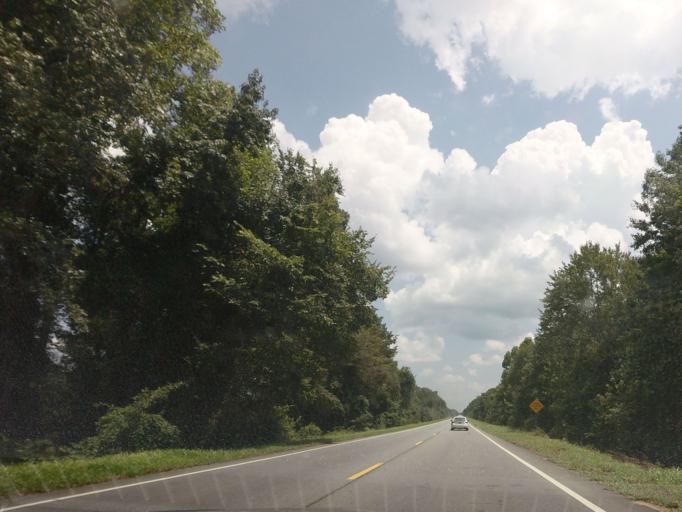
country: US
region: Georgia
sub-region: Houston County
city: Robins Air Force Base
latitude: 32.5432
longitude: -83.5537
